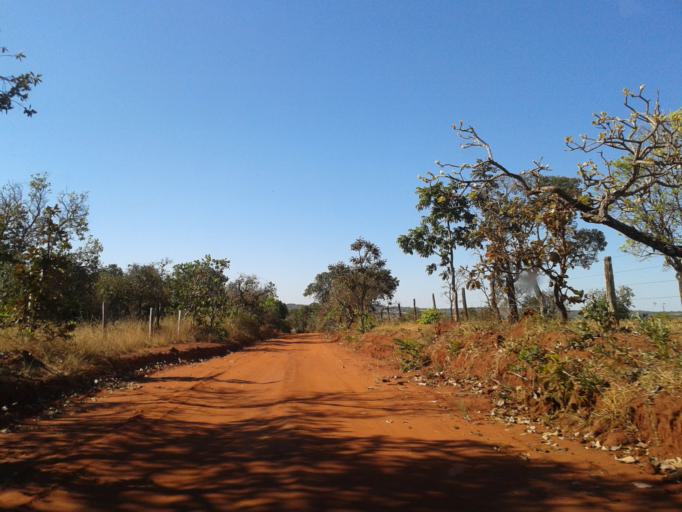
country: BR
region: Minas Gerais
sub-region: Ituiutaba
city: Ituiutaba
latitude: -19.0768
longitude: -49.3367
